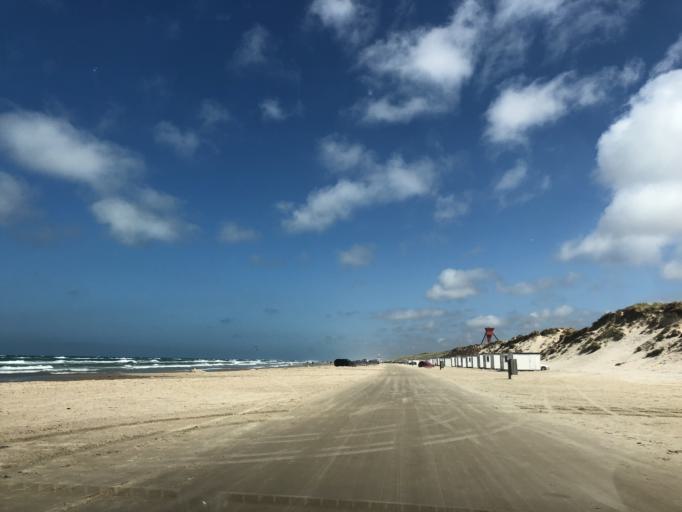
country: DK
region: North Denmark
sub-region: Jammerbugt Kommune
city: Pandrup
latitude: 57.2515
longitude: 9.5751
